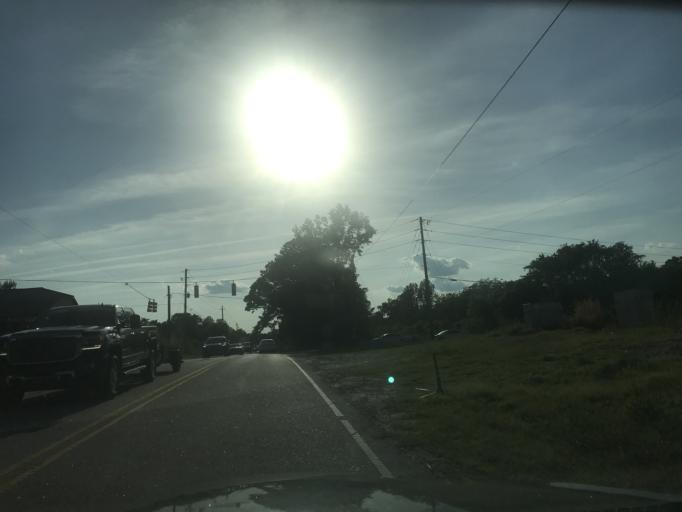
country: US
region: North Carolina
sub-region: Wake County
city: Knightdale
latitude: 35.7469
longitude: -78.4464
